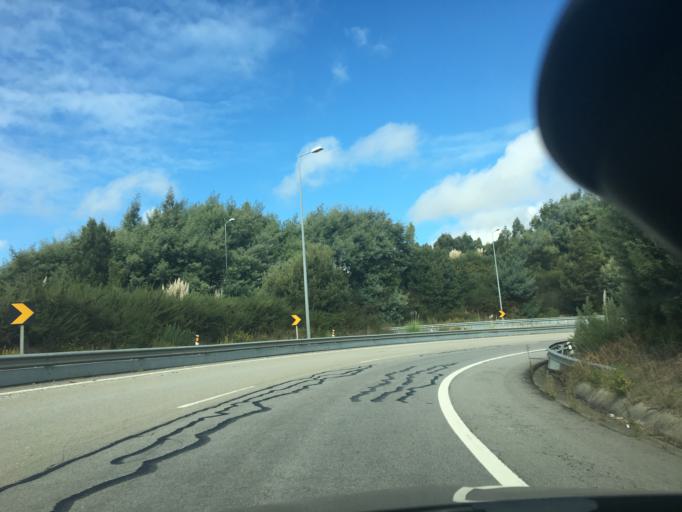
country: PT
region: Porto
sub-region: Matosinhos
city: Santa Cruz do Bispo
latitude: 41.2262
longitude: -8.6670
